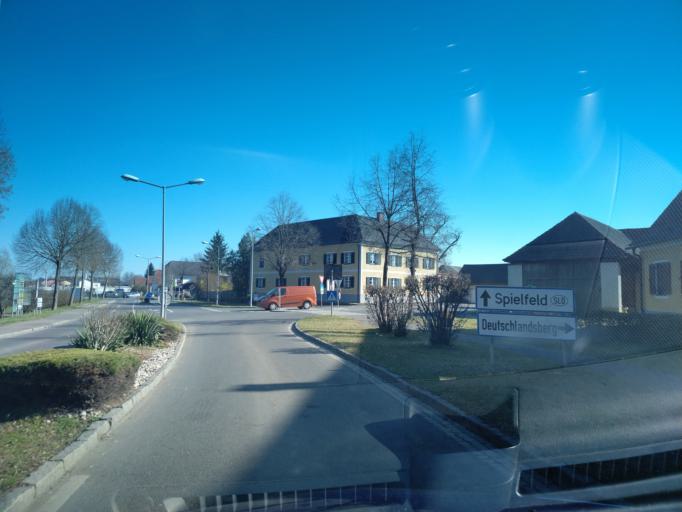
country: AT
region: Styria
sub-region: Politischer Bezirk Leibnitz
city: Stocking
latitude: 46.8620
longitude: 15.5282
